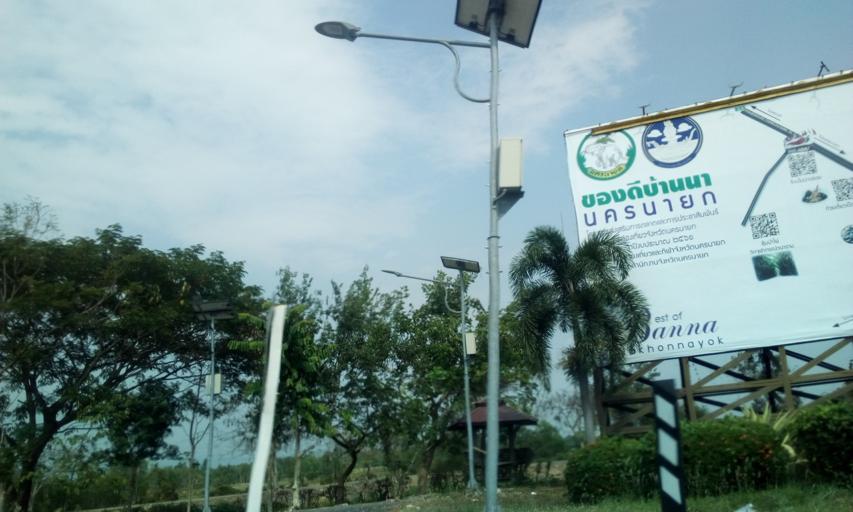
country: TH
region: Nakhon Nayok
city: Nakhon Nayok
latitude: 14.2047
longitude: 101.1884
